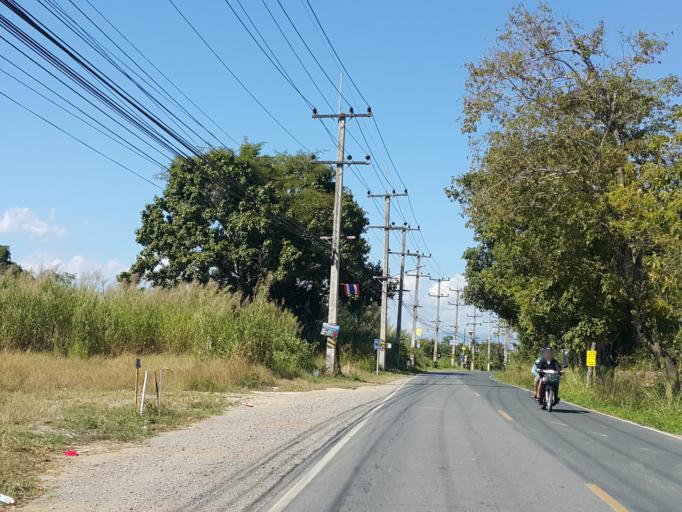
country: TH
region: Chiang Mai
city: San Sai
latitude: 18.9442
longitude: 98.9281
